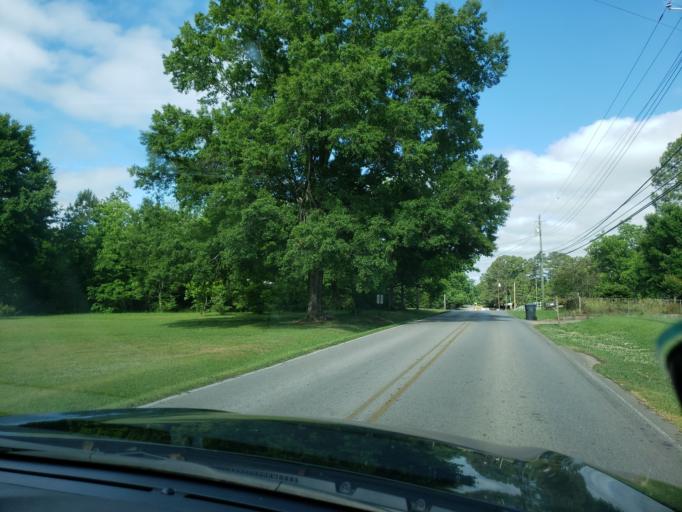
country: US
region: Alabama
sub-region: Calhoun County
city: Weaver
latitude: 33.7517
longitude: -85.8362
